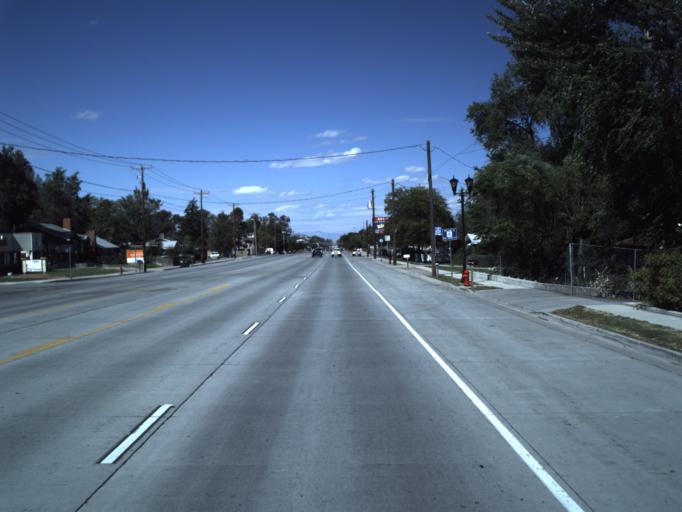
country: US
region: Utah
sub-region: Salt Lake County
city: South Jordan Heights
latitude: 40.5799
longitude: -111.9386
